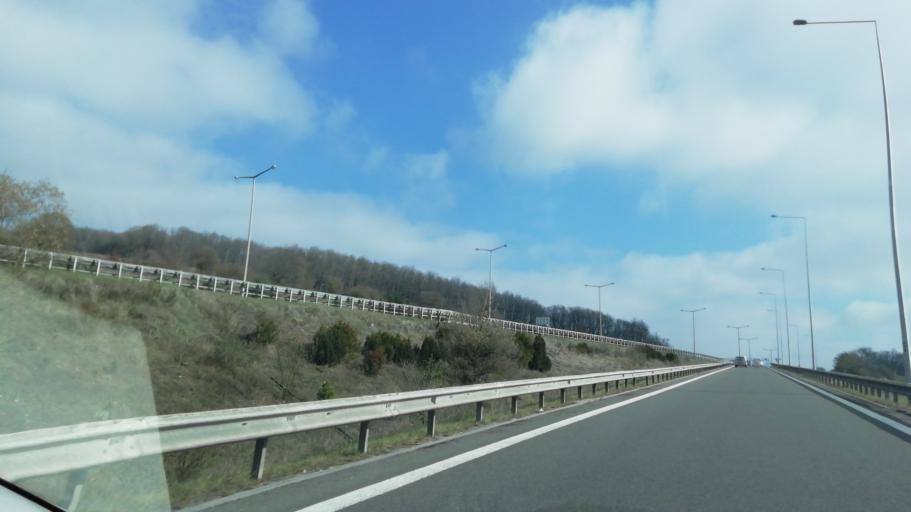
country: TR
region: Bolu
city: Bolu
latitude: 40.7206
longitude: 31.4818
